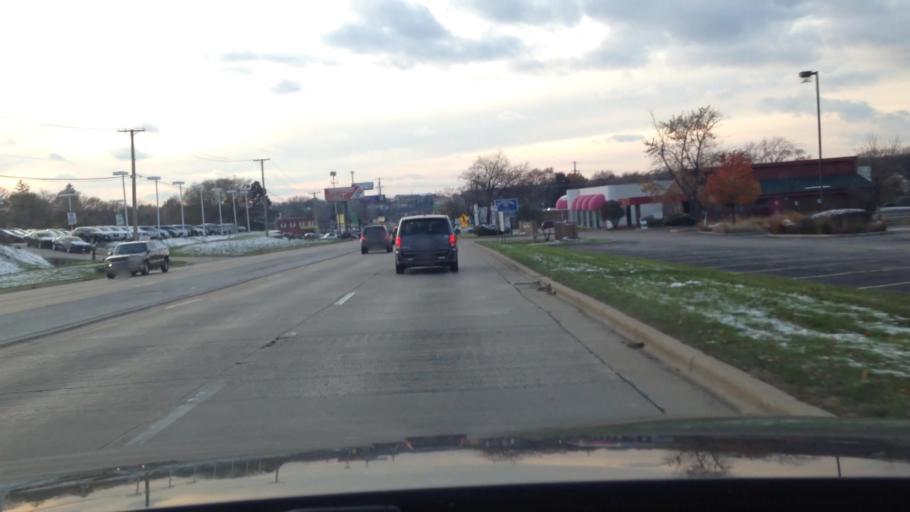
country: US
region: Illinois
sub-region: DuPage County
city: Lombard
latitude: 41.8598
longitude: -88.0305
